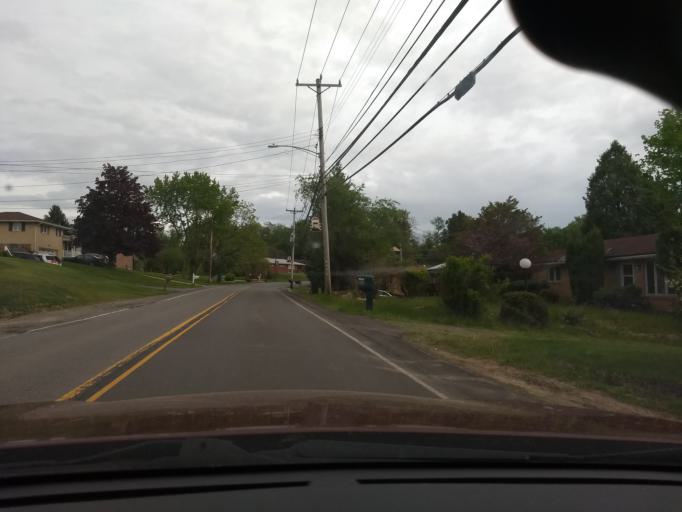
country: US
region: Pennsylvania
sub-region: Allegheny County
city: Rennerdale
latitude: 40.4592
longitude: -80.1385
